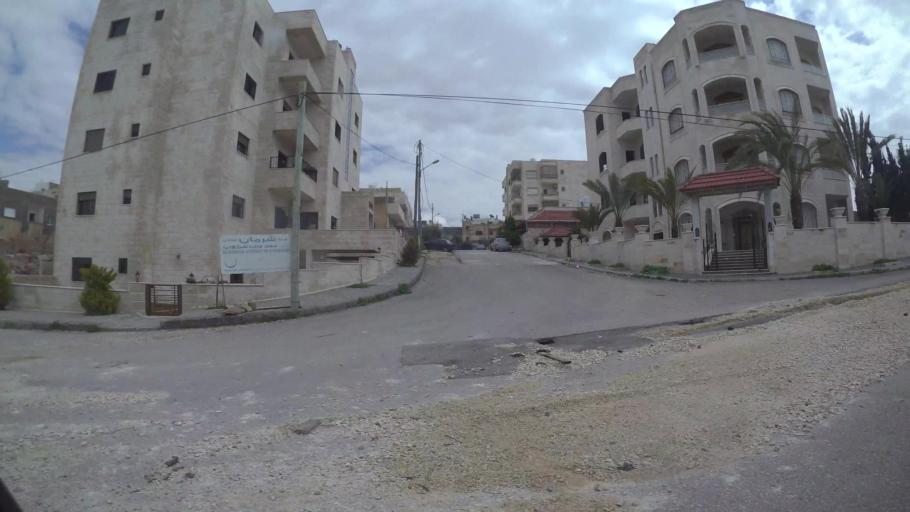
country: JO
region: Amman
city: Al Jubayhah
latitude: 32.0555
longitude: 35.8223
